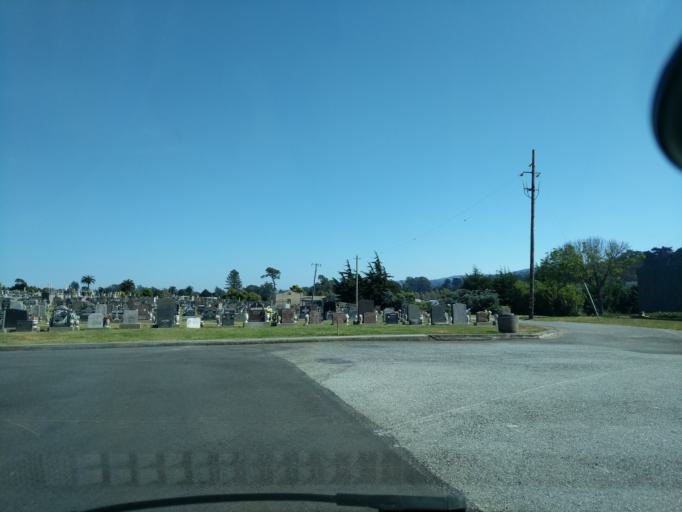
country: US
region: California
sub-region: San Mateo County
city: Colma
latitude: 37.6812
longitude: -122.4610
